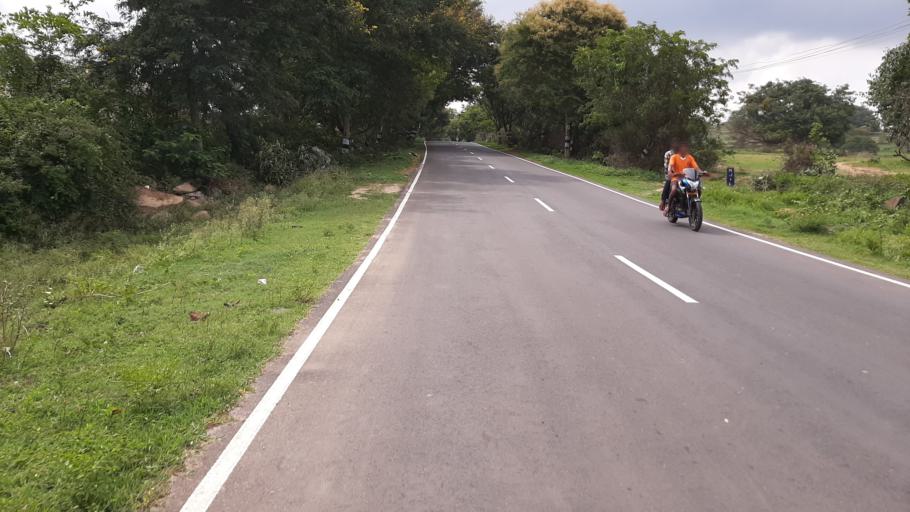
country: IN
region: Tamil Nadu
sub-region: Krishnagiri
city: Denkanikota
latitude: 12.5391
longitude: 77.7660
